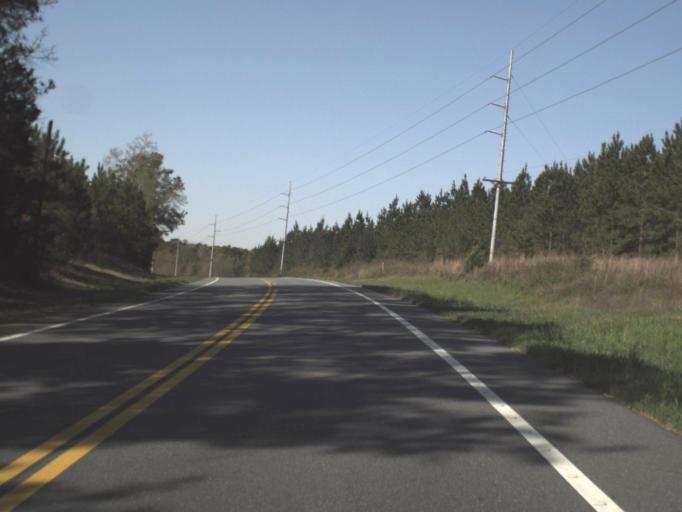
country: US
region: Alabama
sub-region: Houston County
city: Cottonwood
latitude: 30.9443
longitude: -85.2864
